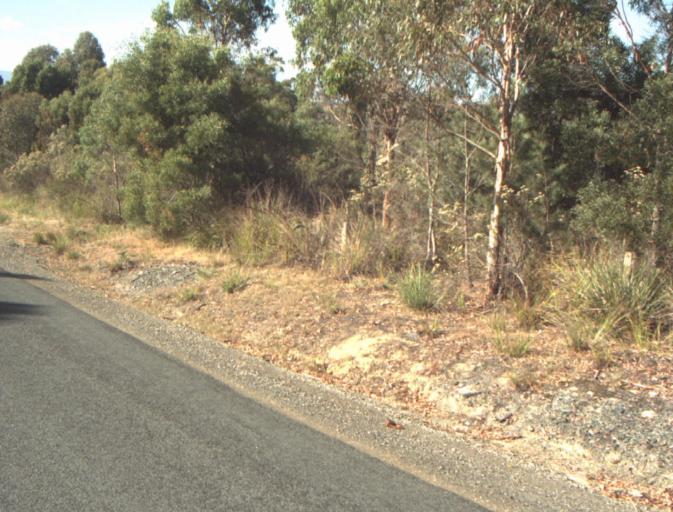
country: AU
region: Tasmania
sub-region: Dorset
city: Bridport
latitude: -41.1391
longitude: 147.2275
